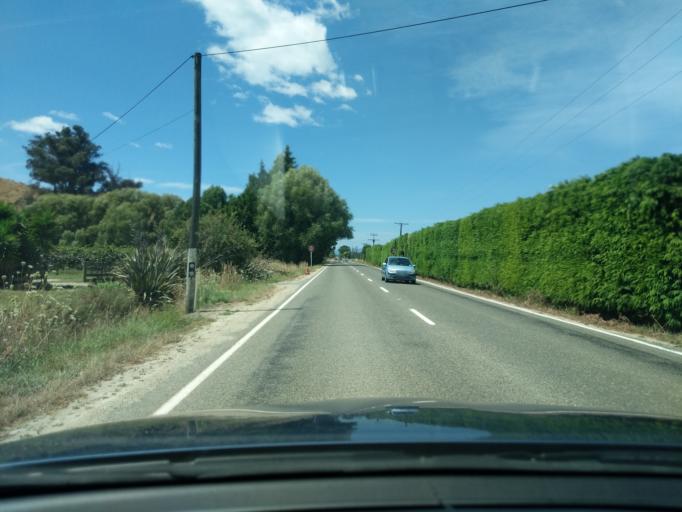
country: NZ
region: Tasman
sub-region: Tasman District
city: Motueka
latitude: -41.0628
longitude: 172.9805
